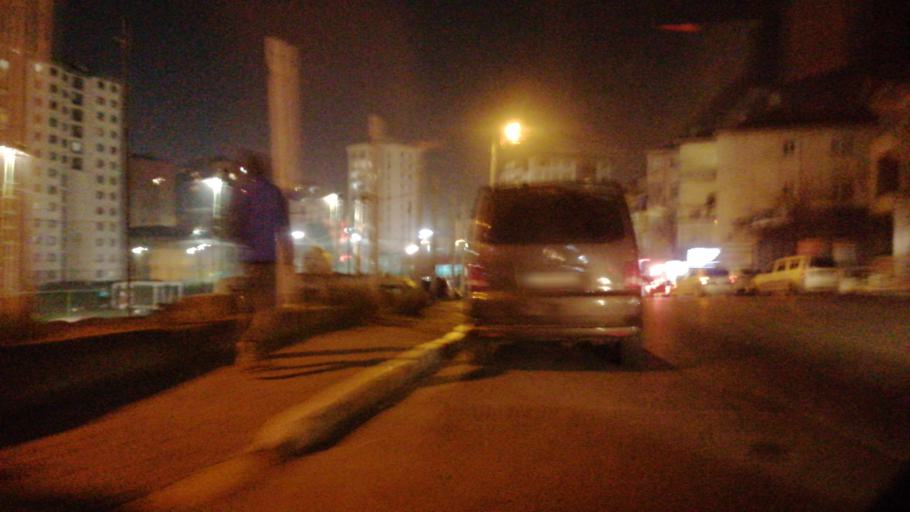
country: TR
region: Istanbul
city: Umraniye
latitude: 41.0164
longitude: 29.1294
